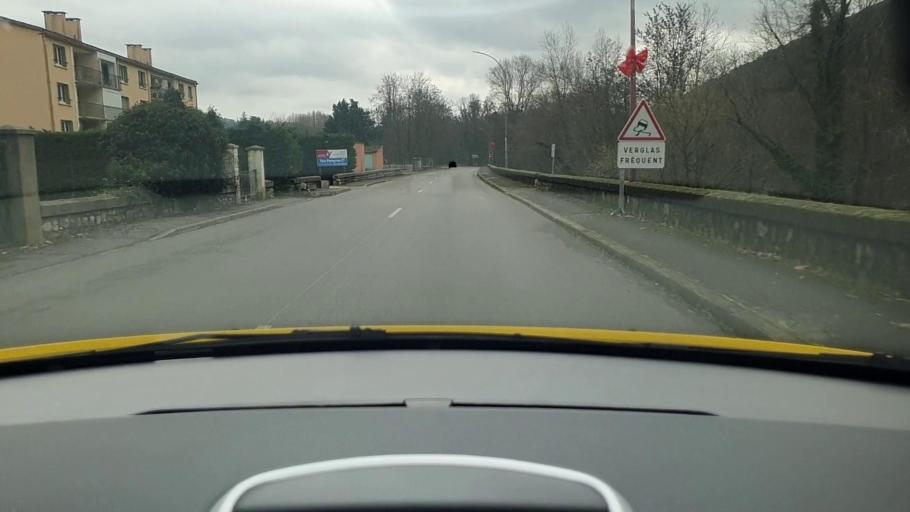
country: FR
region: Languedoc-Roussillon
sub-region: Departement du Gard
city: Besseges
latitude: 44.2875
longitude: 4.1071
